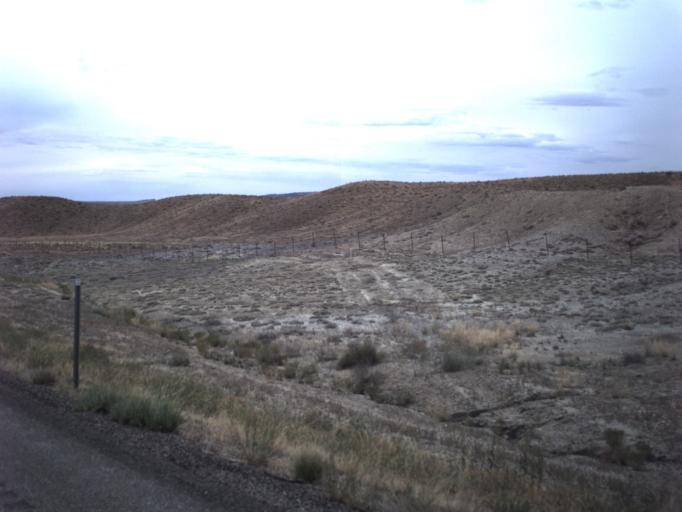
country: US
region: Utah
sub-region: Carbon County
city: East Carbon City
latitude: 39.2753
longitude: -110.3473
